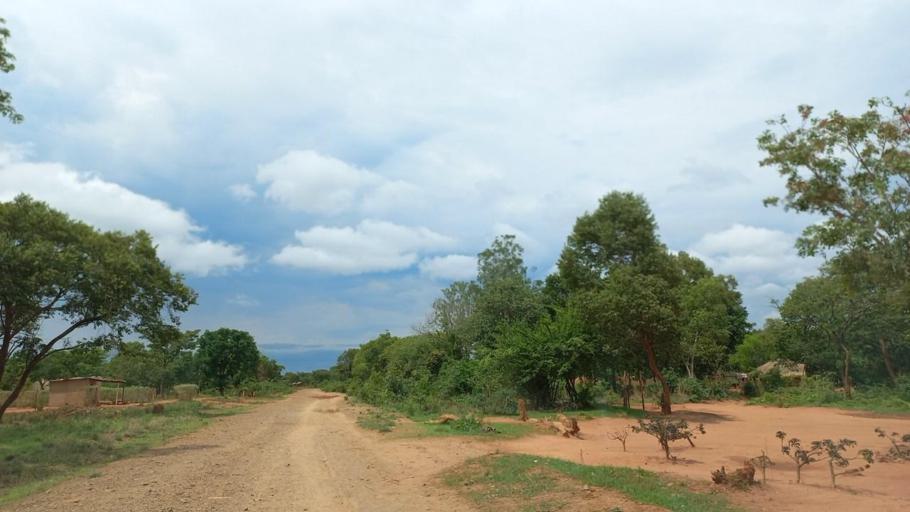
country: ZM
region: North-Western
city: Kalengwa
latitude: -13.4644
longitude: 25.0073
